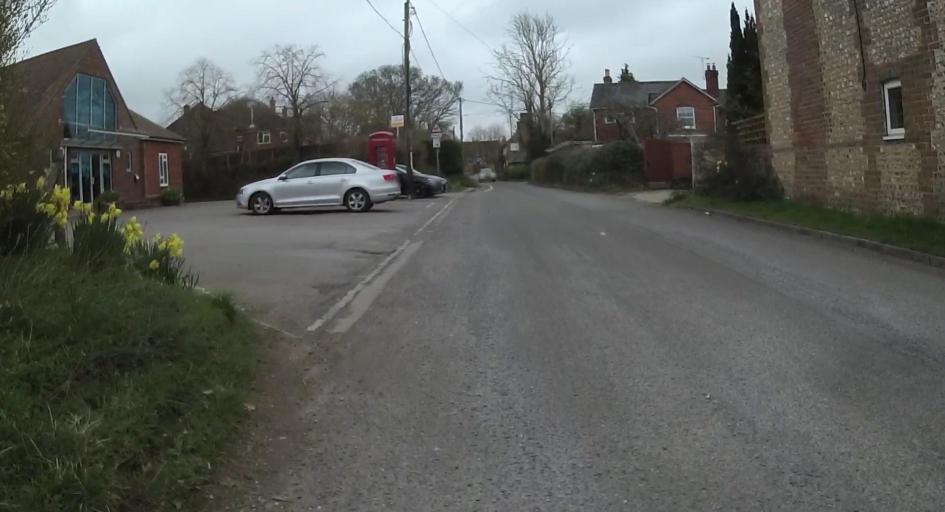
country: GB
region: England
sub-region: Hampshire
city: Four Marks
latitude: 51.0832
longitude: -1.0839
